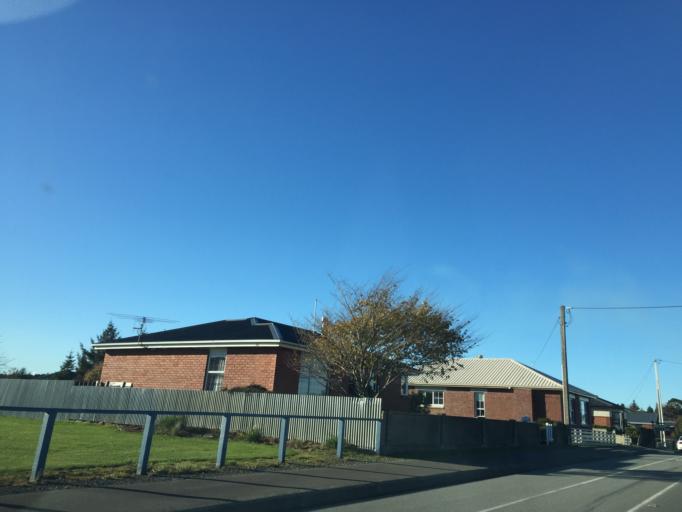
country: NZ
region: Southland
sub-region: Invercargill City
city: Invercargill
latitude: -46.3755
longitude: 168.3493
